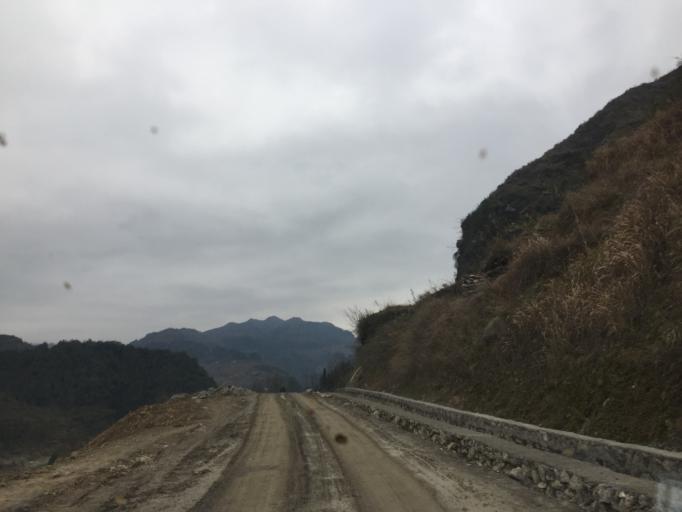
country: CN
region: Guizhou Sheng
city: Changfeng
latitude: 28.4410
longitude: 108.0790
